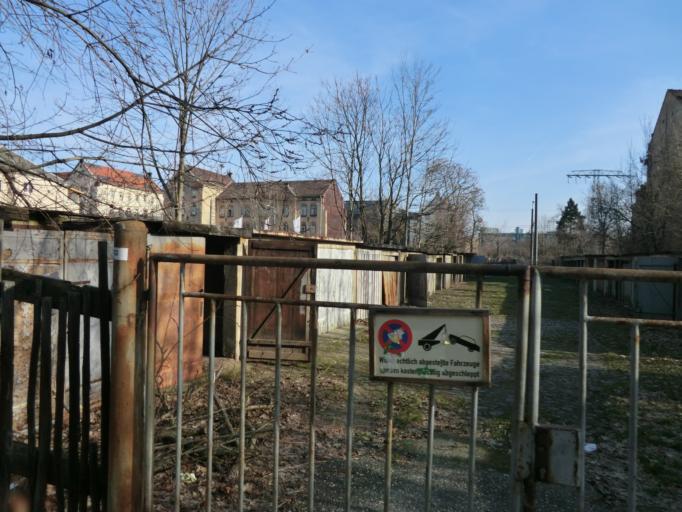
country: DE
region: Saxony
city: Dresden
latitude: 51.0495
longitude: 13.7106
